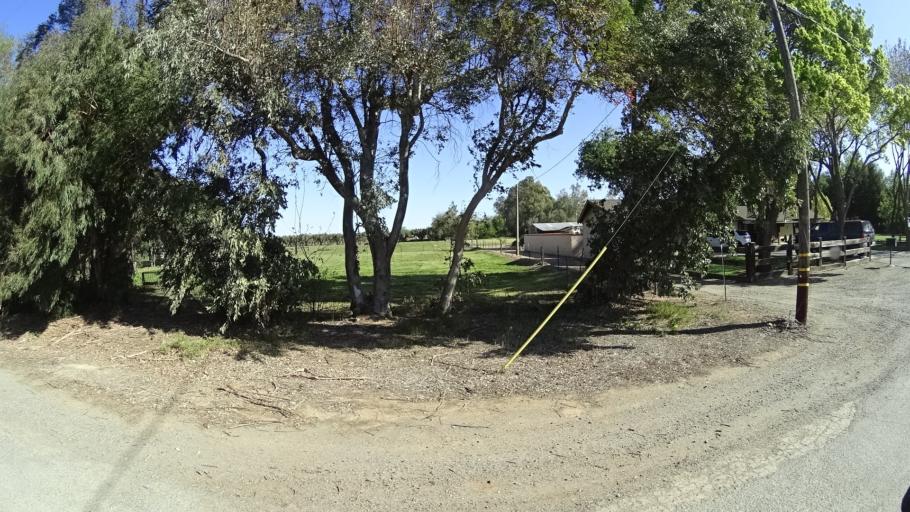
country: US
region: California
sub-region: Glenn County
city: Orland
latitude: 39.7114
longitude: -122.2186
